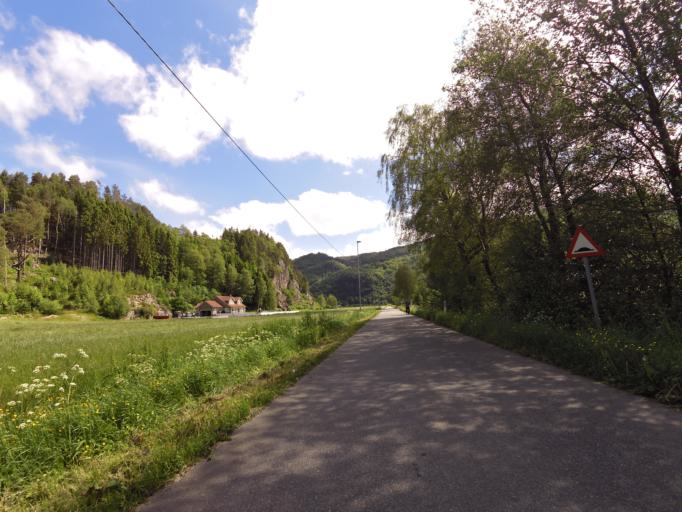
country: NO
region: Vest-Agder
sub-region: Kvinesdal
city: Liknes
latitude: 58.3053
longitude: 6.9437
